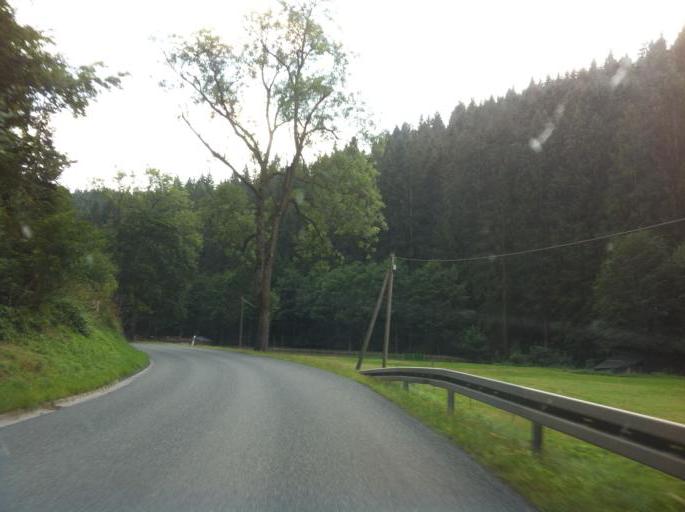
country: DE
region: Thuringia
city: Katzhutte
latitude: 50.5413
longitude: 11.0648
